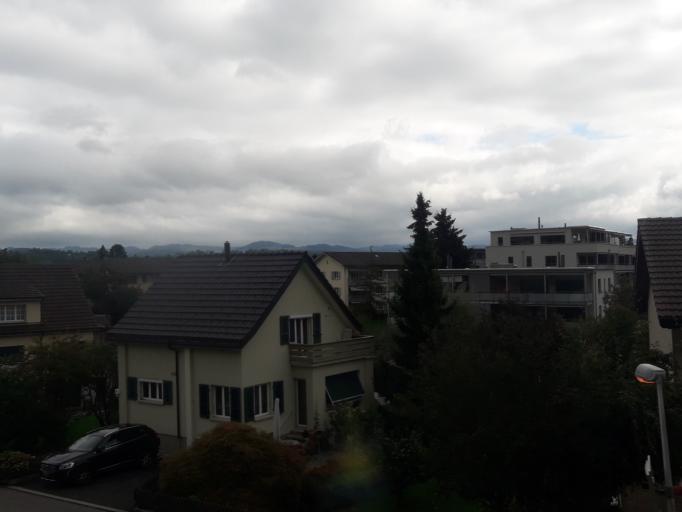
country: CH
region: Bern
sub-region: Bern-Mittelland District
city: Belp
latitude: 46.8928
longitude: 7.4954
